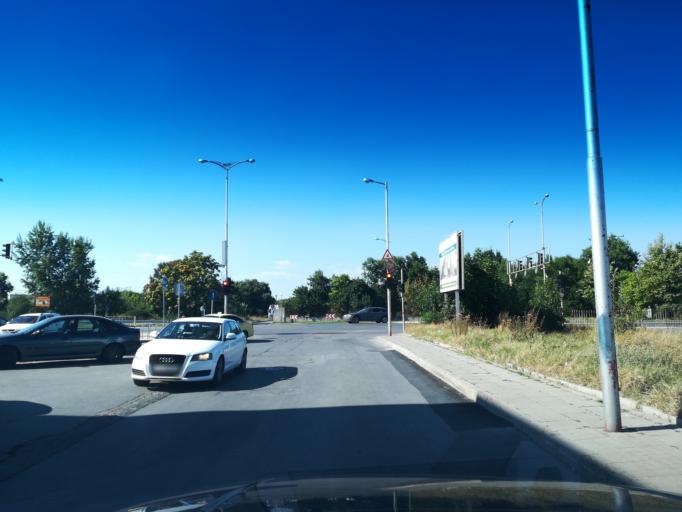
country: BG
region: Plovdiv
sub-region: Obshtina Plovdiv
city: Plovdiv
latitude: 42.1555
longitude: 24.7131
